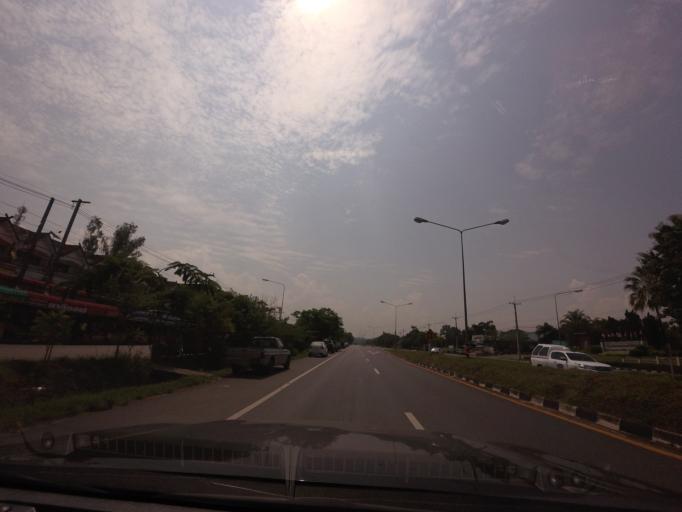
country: TH
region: Phrae
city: Den Chai
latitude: 17.9659
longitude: 100.0662
